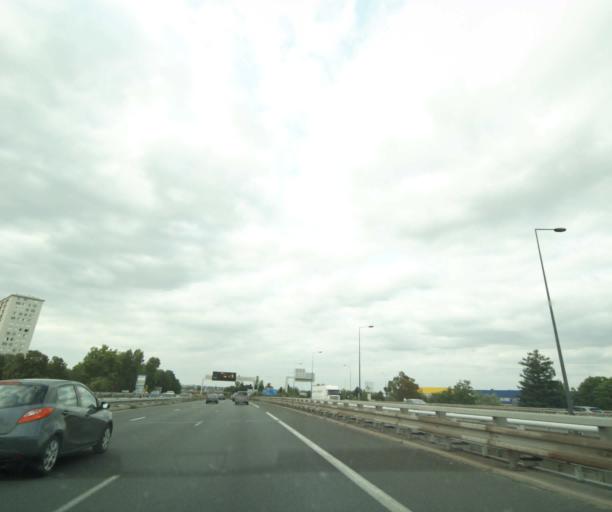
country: FR
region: Centre
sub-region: Departement d'Indre-et-Loire
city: Saint-Avertin
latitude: 47.3734
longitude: 0.7156
